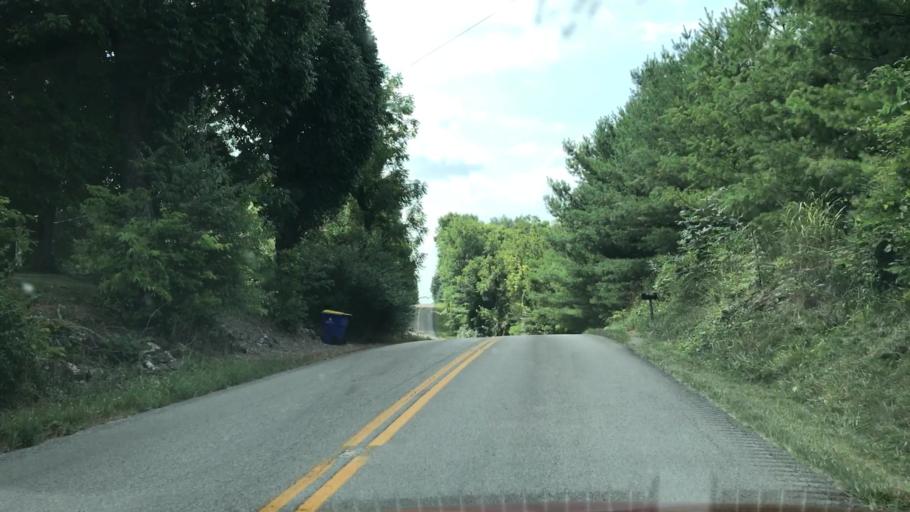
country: US
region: Kentucky
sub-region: Barren County
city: Glasgow
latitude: 36.9655
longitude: -85.8911
